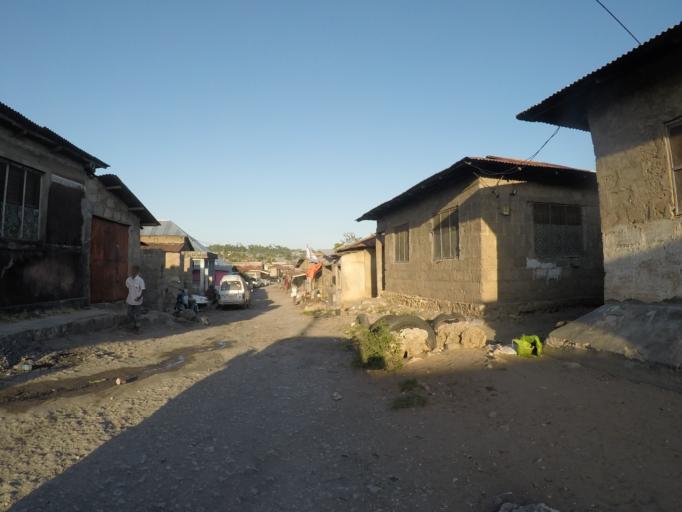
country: TZ
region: Zanzibar Urban/West
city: Zanzibar
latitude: -6.1581
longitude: 39.2156
